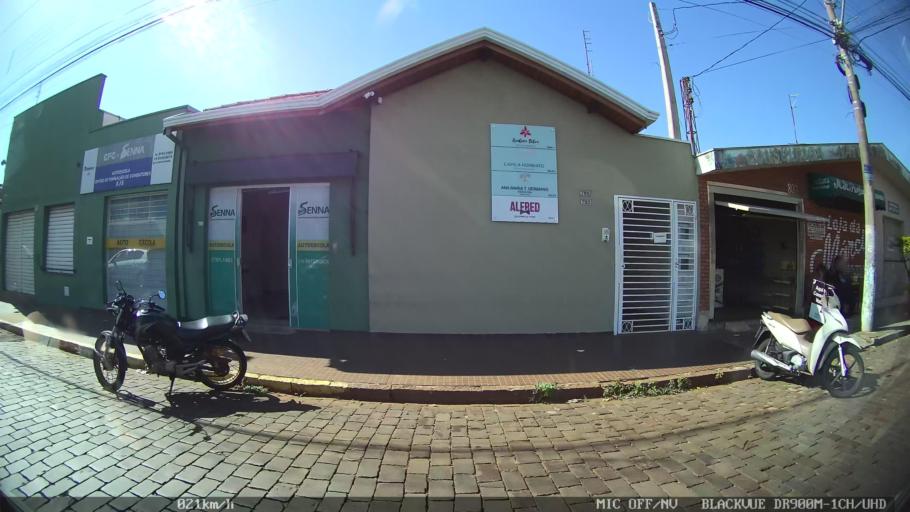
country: BR
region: Sao Paulo
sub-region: Batatais
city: Batatais
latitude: -20.8961
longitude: -47.5837
